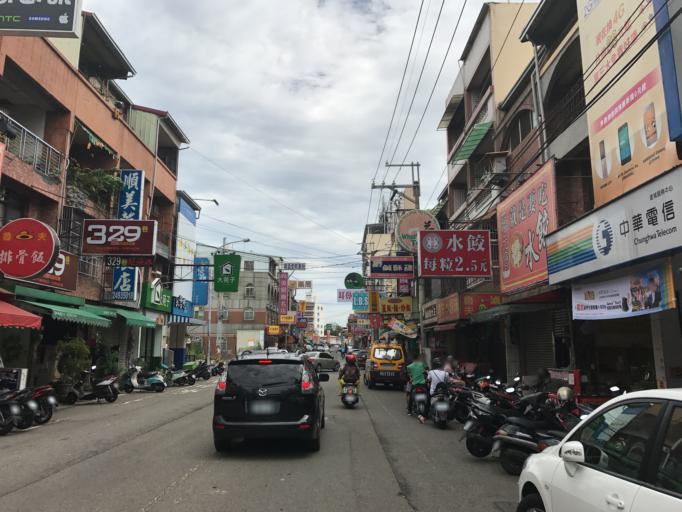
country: TW
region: Taiwan
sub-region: Taichung City
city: Taichung
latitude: 24.0896
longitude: 120.7030
